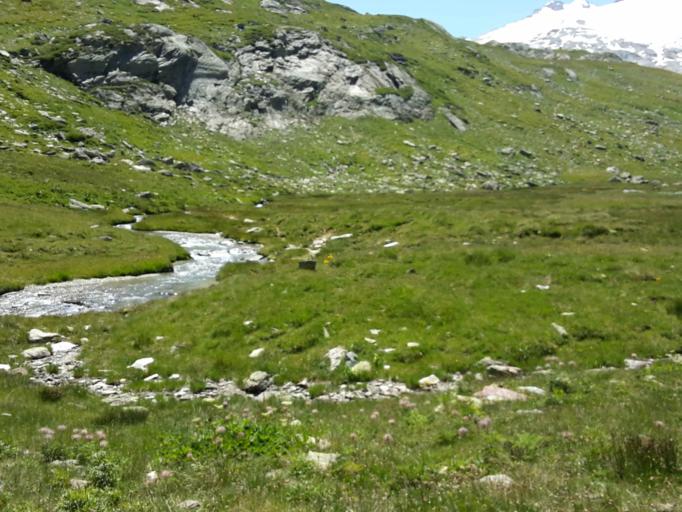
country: IT
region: Aosta Valley
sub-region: Valle d'Aosta
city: Valgrisenche
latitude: 45.6772
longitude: 7.0542
